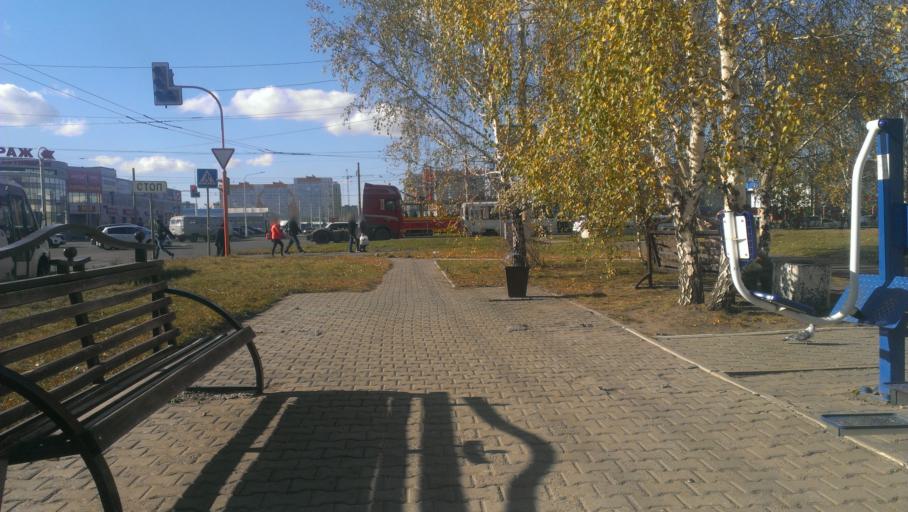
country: RU
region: Altai Krai
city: Novosilikatnyy
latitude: 53.3362
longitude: 83.6701
